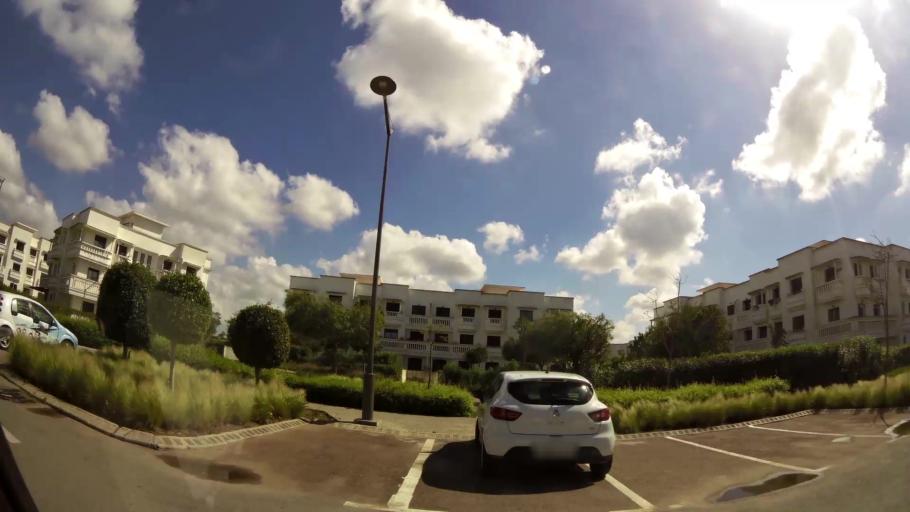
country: MA
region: Grand Casablanca
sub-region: Nouaceur
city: Bouskoura
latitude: 33.4704
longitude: -7.6076
